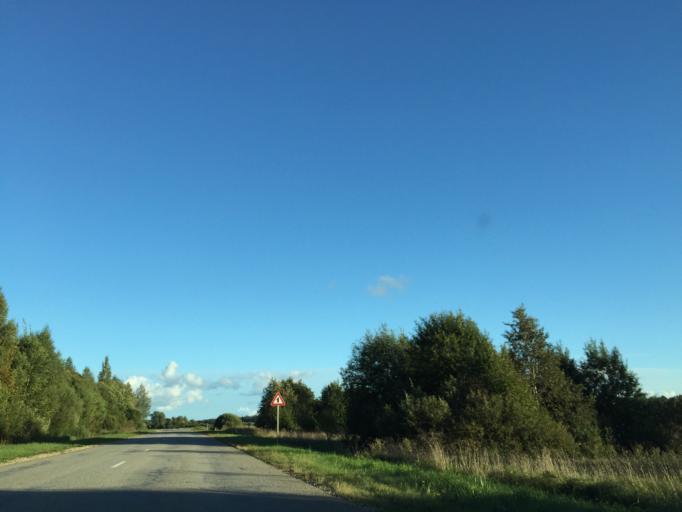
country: LV
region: Kuldigas Rajons
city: Kuldiga
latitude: 56.9400
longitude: 22.0255
